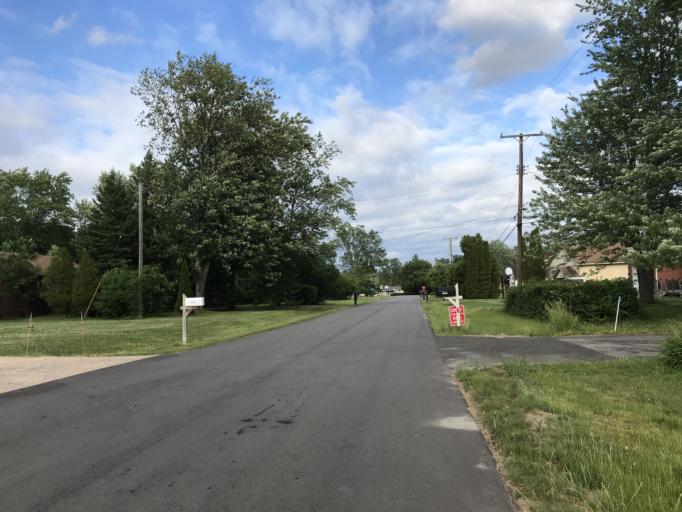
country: US
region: Michigan
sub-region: Oakland County
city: Farmington
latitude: 42.4747
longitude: -83.3398
